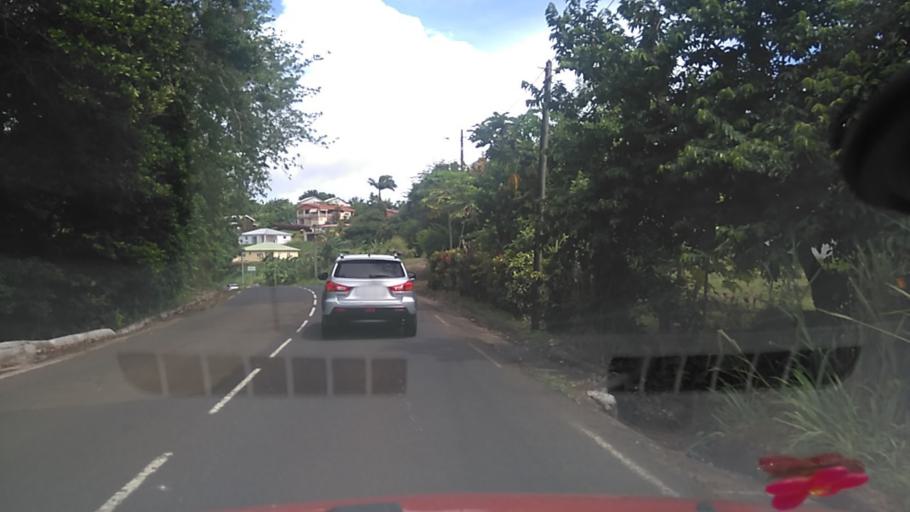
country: MQ
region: Martinique
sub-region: Martinique
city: Le Francois
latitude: 14.5965
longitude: -60.9254
